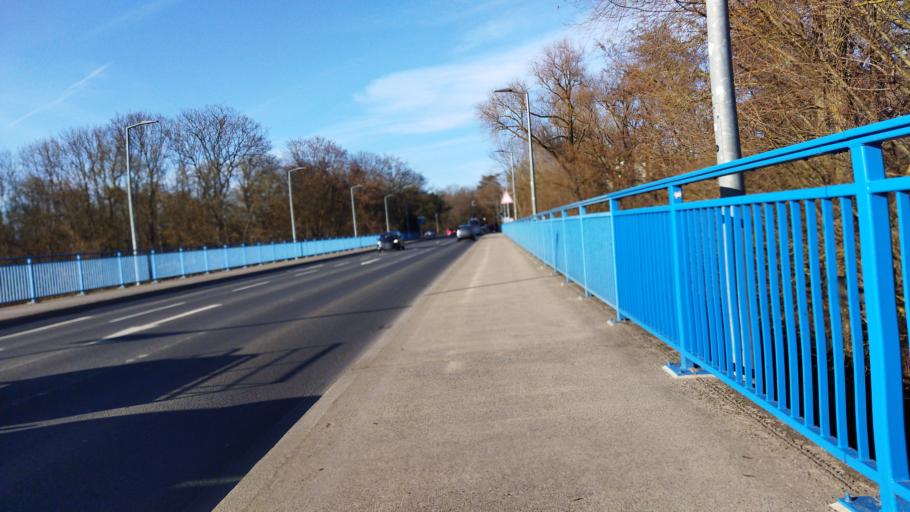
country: DE
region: Bavaria
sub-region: Regierungsbezirk Unterfranken
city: Sennfeld
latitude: 50.0393
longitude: 10.2401
